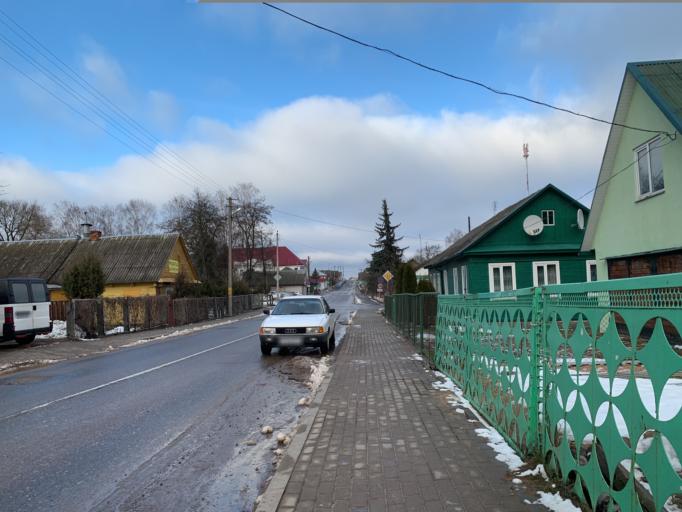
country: BY
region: Minsk
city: Nyasvizh
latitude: 53.2205
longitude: 26.6725
